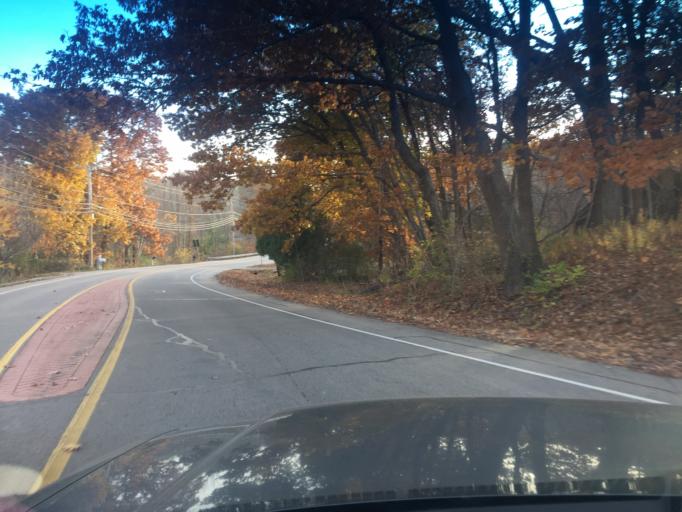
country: US
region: Maine
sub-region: York County
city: York Harbor
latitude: 43.1537
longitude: -70.6367
